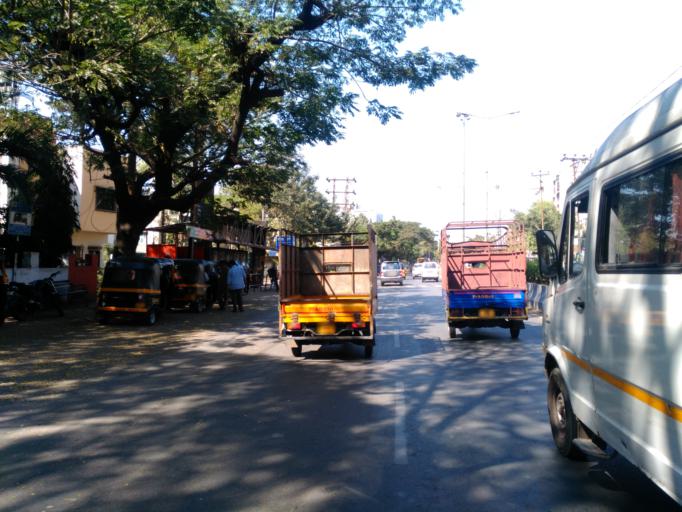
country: IN
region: Maharashtra
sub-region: Pune Division
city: Pune
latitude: 18.4721
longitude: 73.8632
